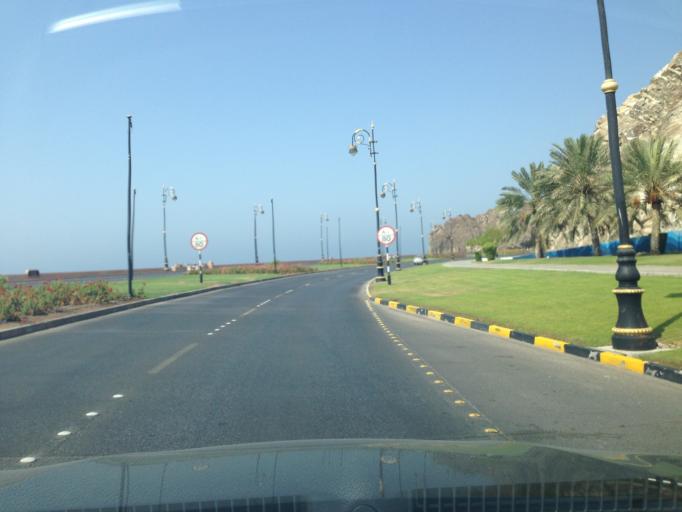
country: OM
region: Muhafazat Masqat
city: Muscat
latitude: 23.6207
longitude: 58.5680
